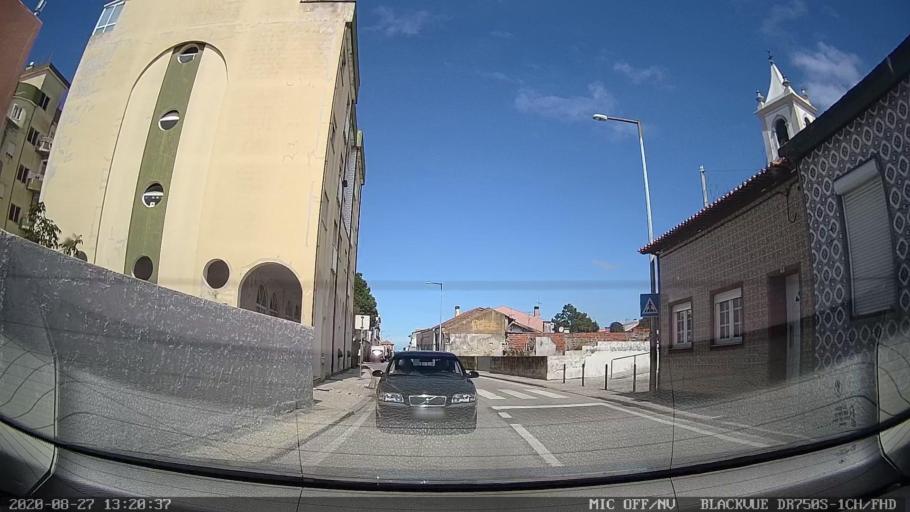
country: PT
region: Aveiro
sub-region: Vagos
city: Vagos
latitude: 40.5558
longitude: -8.6814
